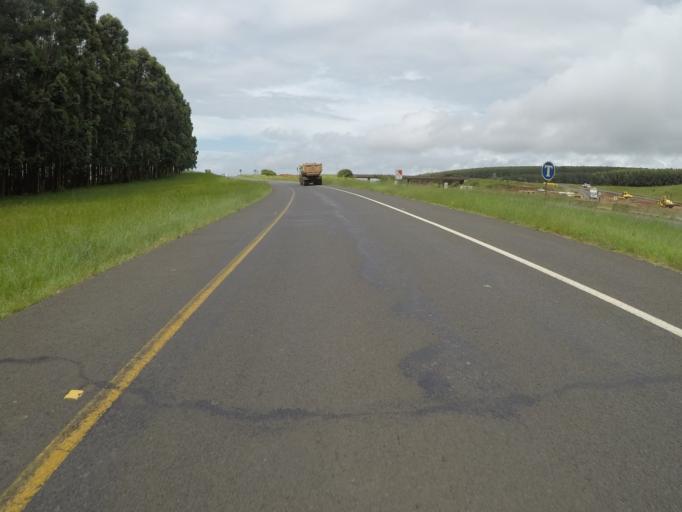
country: ZA
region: KwaZulu-Natal
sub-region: uThungulu District Municipality
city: eSikhawini
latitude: -28.8631
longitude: 31.8875
